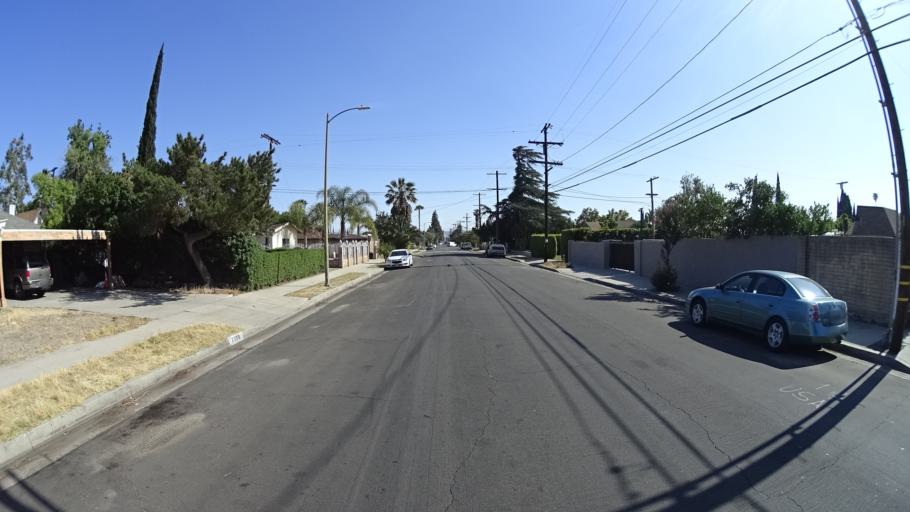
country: US
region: California
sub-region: Los Angeles County
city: Van Nuys
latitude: 34.2112
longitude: -118.4172
